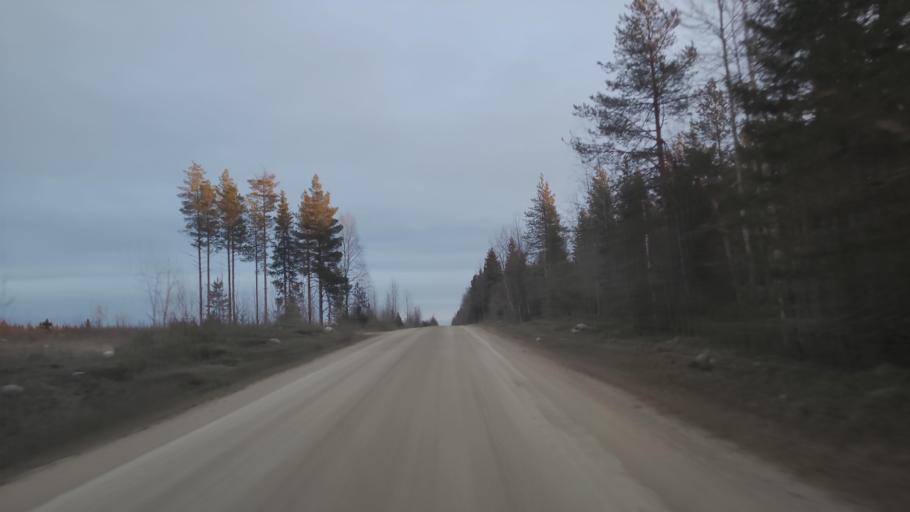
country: FI
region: Lapland
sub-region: Kemi-Tornio
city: Tervola
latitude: 66.0598
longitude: 24.9357
